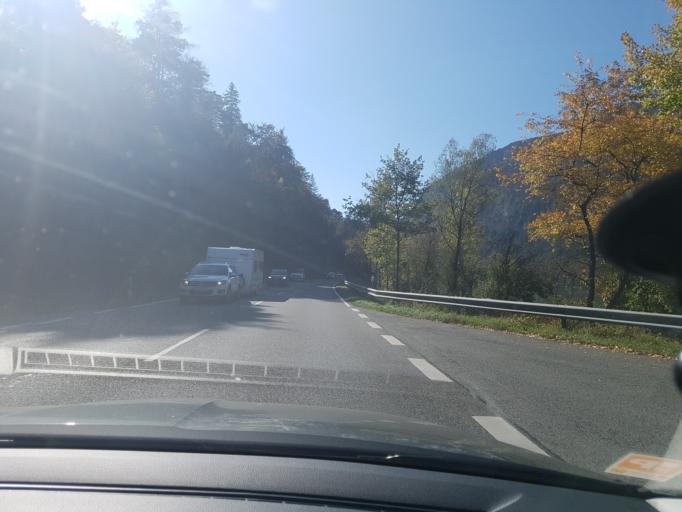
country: DE
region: Bavaria
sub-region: Upper Bavaria
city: Bad Reichenhall
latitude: 47.7090
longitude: 12.8617
